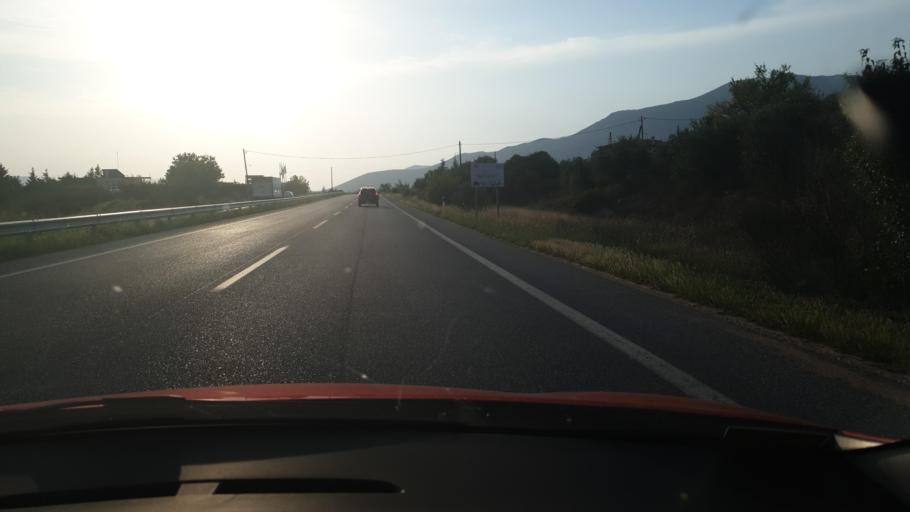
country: GR
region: Central Macedonia
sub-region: Nomos Chalkidikis
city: Galatista
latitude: 40.4649
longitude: 23.2614
